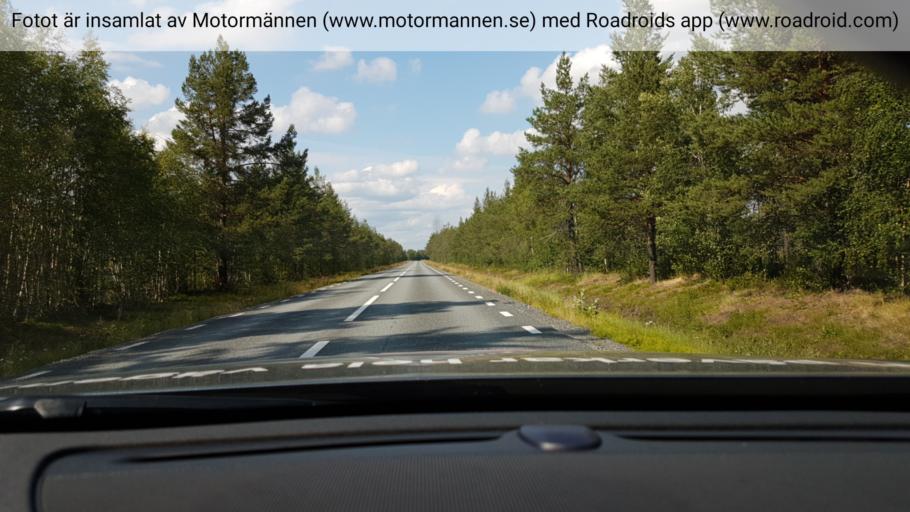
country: SE
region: Vaesterbotten
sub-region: Sorsele Kommun
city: Sorsele
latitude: 65.5046
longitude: 17.5458
